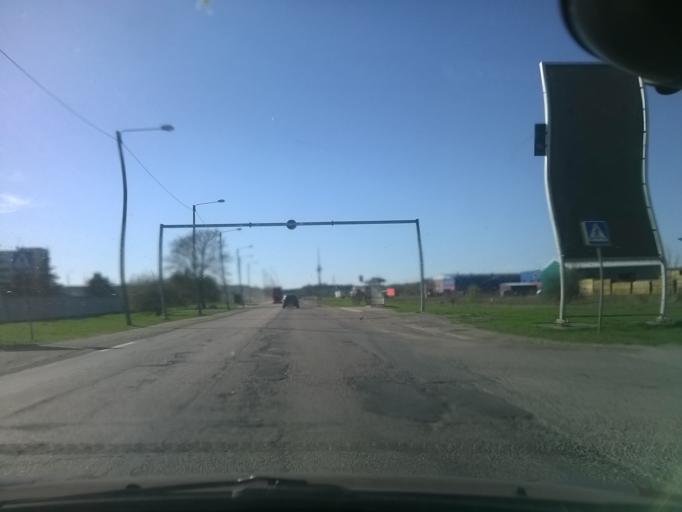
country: EE
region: Harju
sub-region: Joelaehtme vald
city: Loo
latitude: 59.4573
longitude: 24.9396
